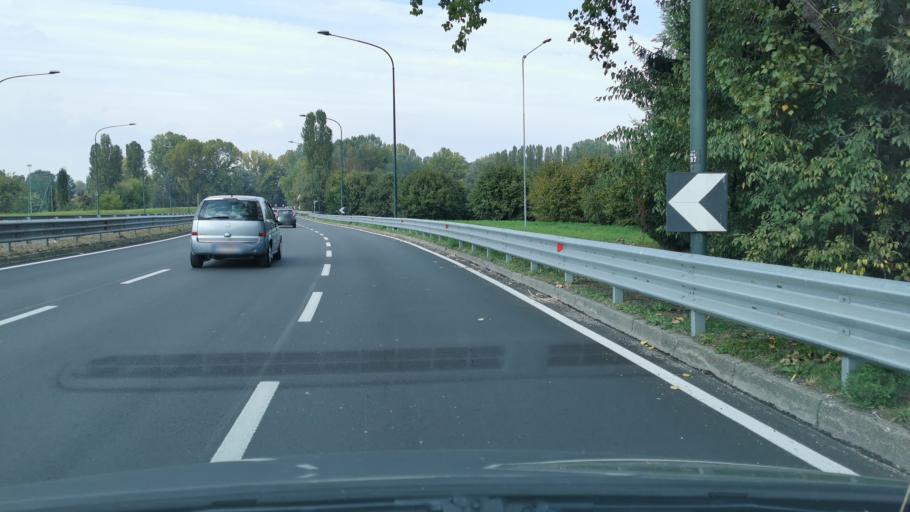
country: IT
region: Piedmont
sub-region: Provincia di Torino
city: San Mauro Torinese
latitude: 45.0857
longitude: 7.7287
